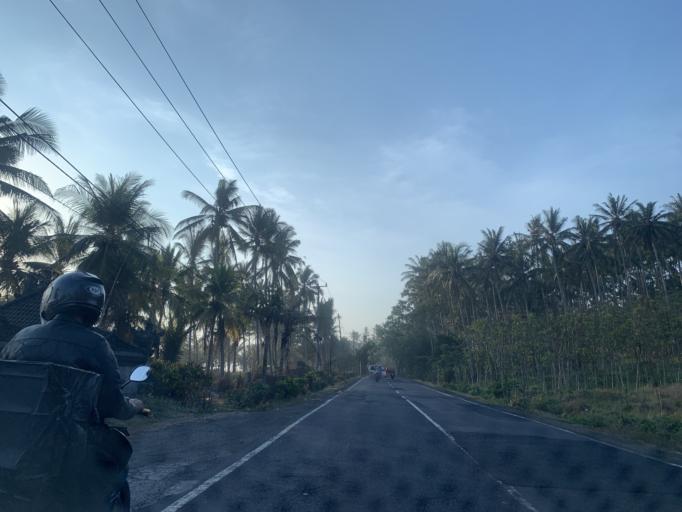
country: ID
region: Bali
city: Banjar Swastika
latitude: -8.4647
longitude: 114.9130
